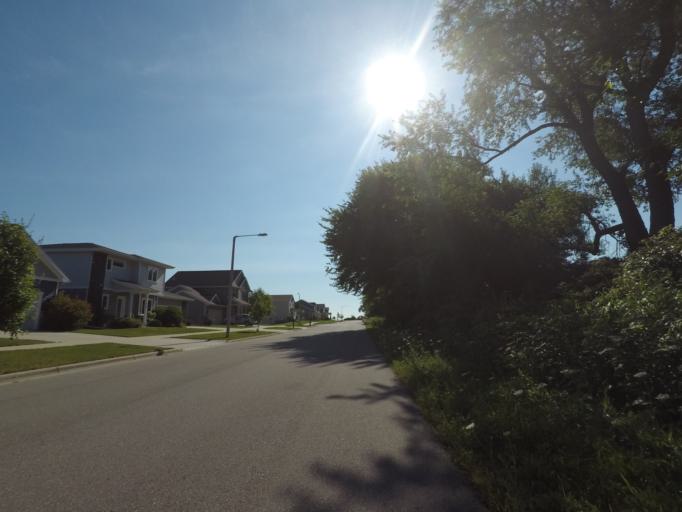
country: US
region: Wisconsin
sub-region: Dane County
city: Middleton
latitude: 43.0639
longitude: -89.5498
